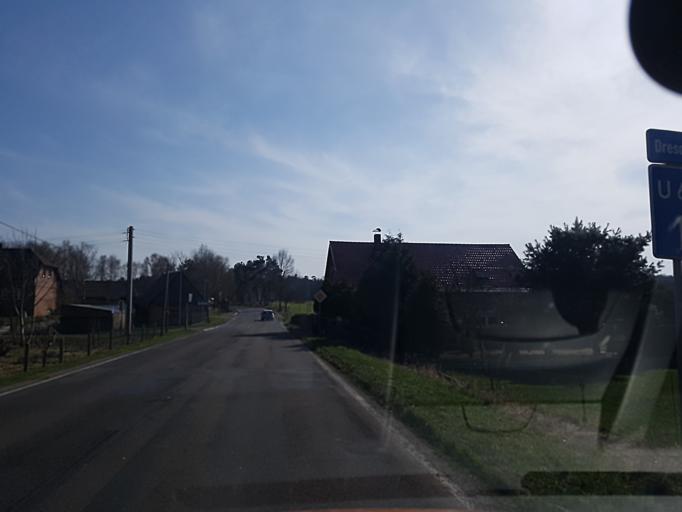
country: DE
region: Brandenburg
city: Bronkow
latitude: 51.7041
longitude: 13.9196
